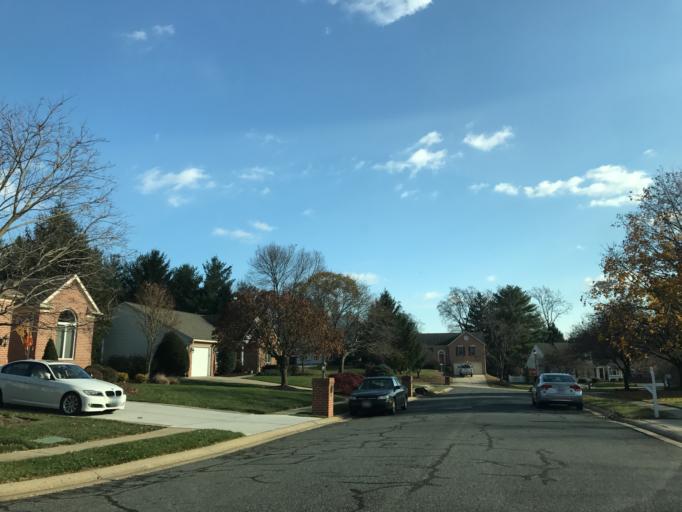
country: US
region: Maryland
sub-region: Harford County
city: North Bel Air
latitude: 39.5416
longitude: -76.3611
